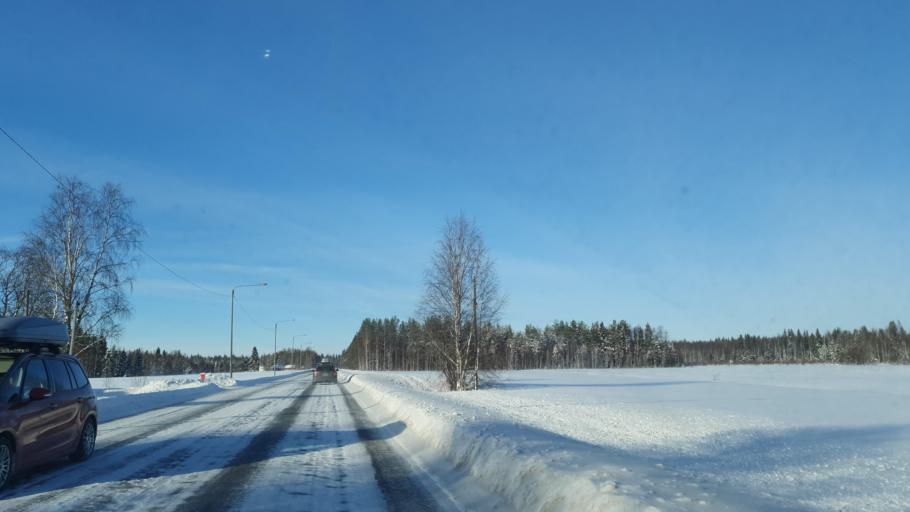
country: FI
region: Lapland
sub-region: Kemi-Tornio
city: Tornio
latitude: 66.0852
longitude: 23.9642
